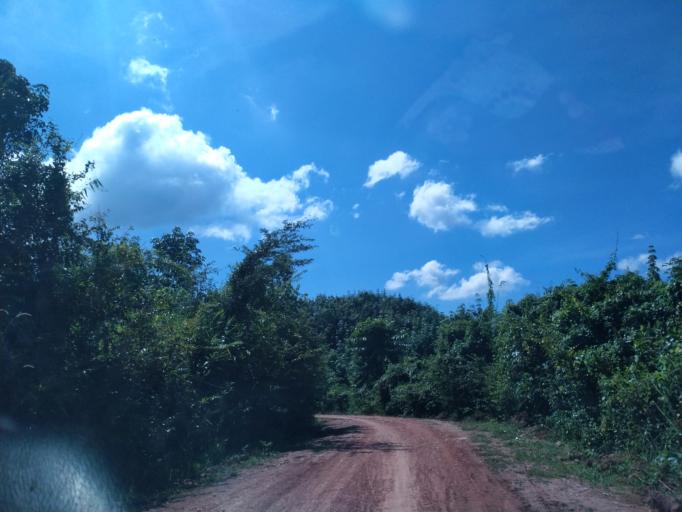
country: LA
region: Vientiane
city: Muang Phon-Hong
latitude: 18.6131
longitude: 102.8508
